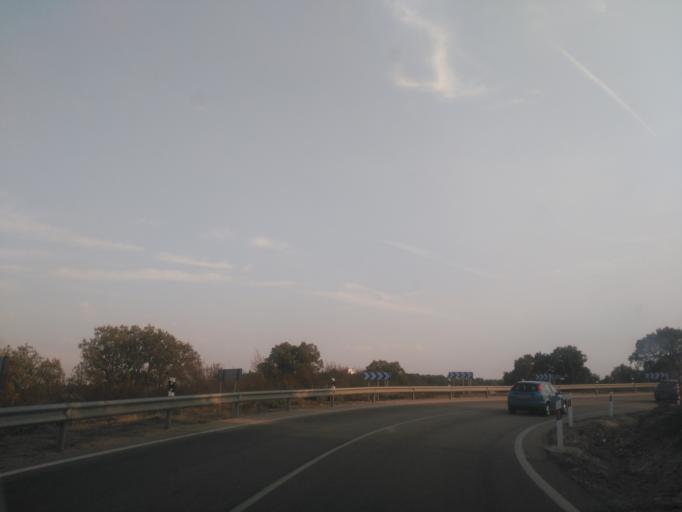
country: ES
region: Castille and Leon
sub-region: Provincia de Zamora
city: Montamarta
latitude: 41.7016
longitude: -5.8149
